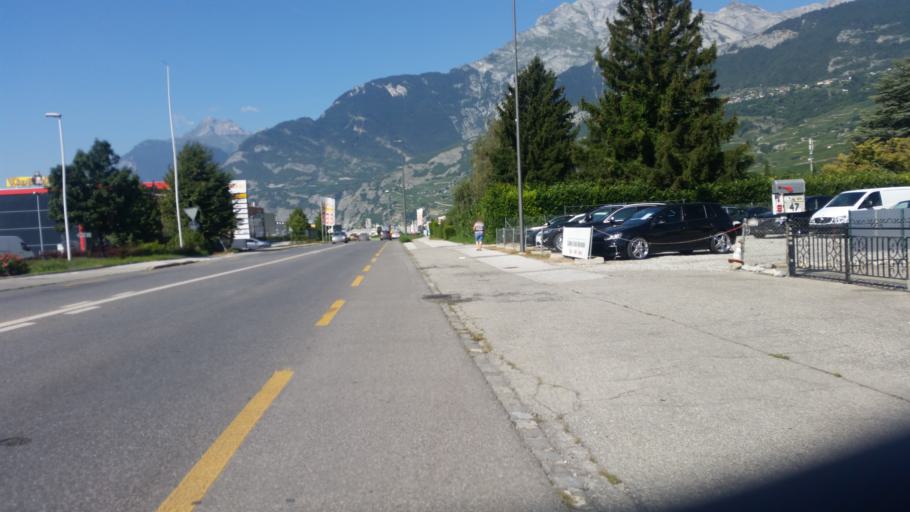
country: CH
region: Valais
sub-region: Conthey District
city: Conthey
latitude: 46.2245
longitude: 7.3067
